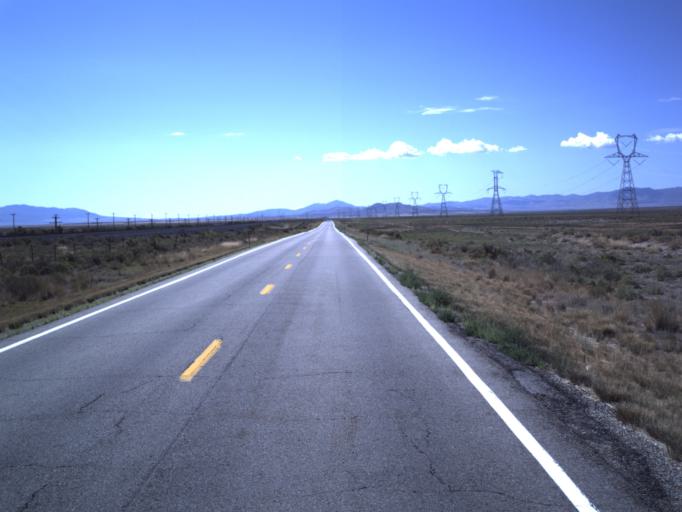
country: US
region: Utah
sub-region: Tooele County
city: Tooele
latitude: 40.3032
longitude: -112.4031
